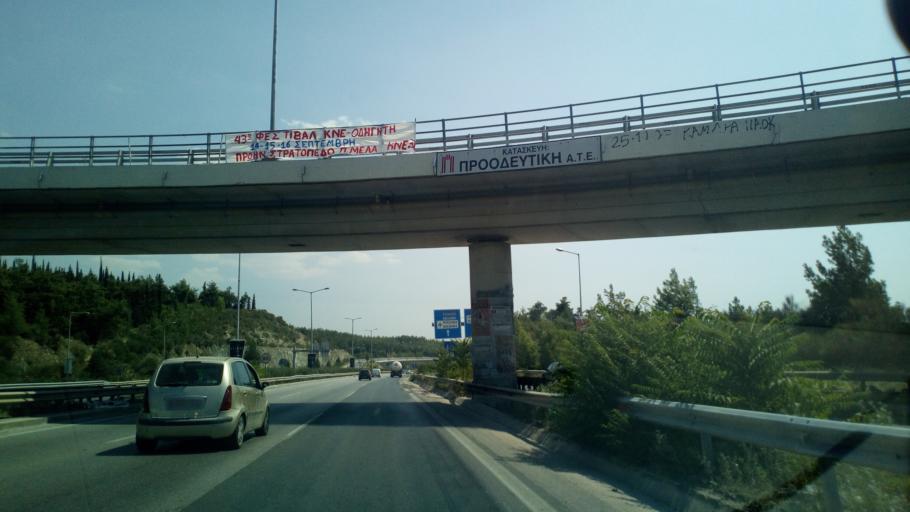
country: GR
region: Central Macedonia
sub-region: Nomos Thessalonikis
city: Triandria
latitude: 40.6262
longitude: 22.9789
